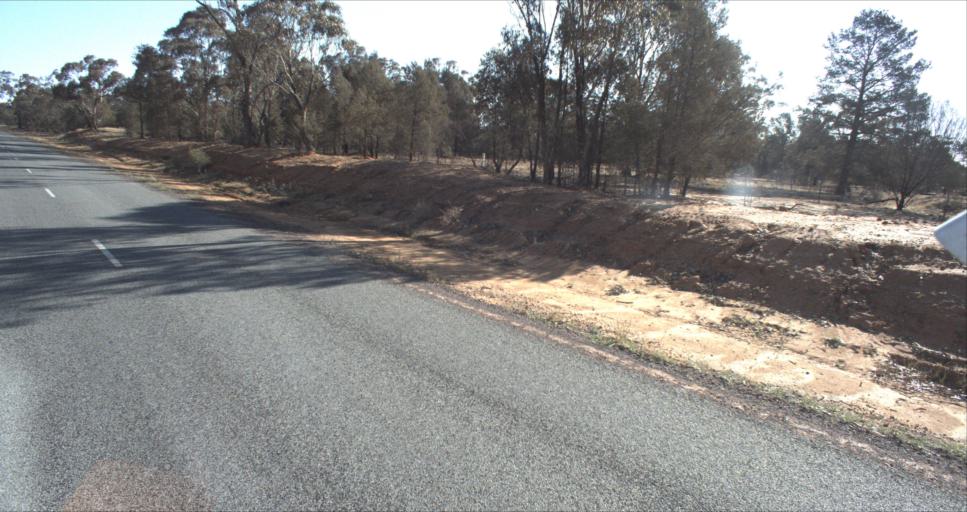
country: AU
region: New South Wales
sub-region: Leeton
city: Leeton
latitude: -34.6486
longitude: 146.3517
